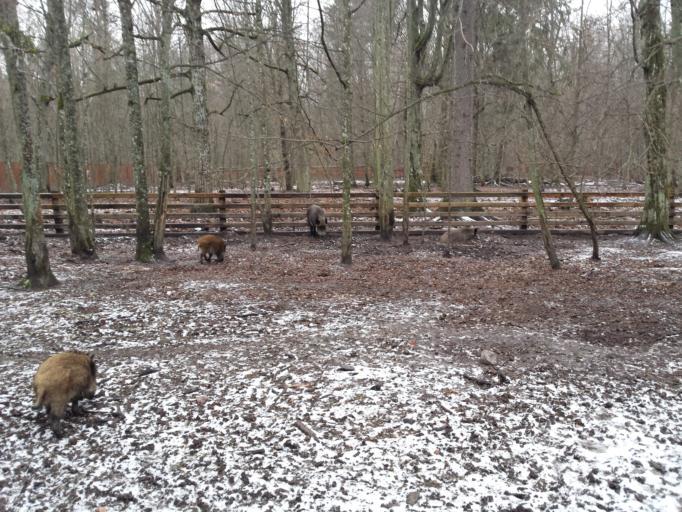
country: PL
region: Podlasie
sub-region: Powiat hajnowski
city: Bialowieza
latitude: 52.7074
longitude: 23.8000
